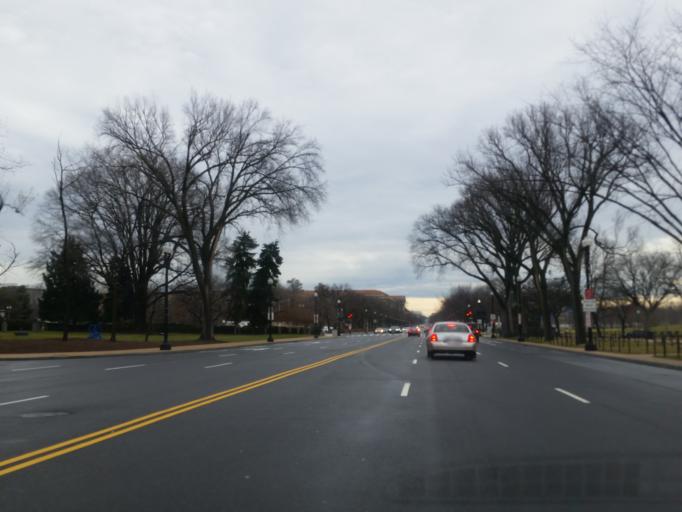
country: US
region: Washington, D.C.
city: Washington, D.C.
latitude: 38.8921
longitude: -77.0413
